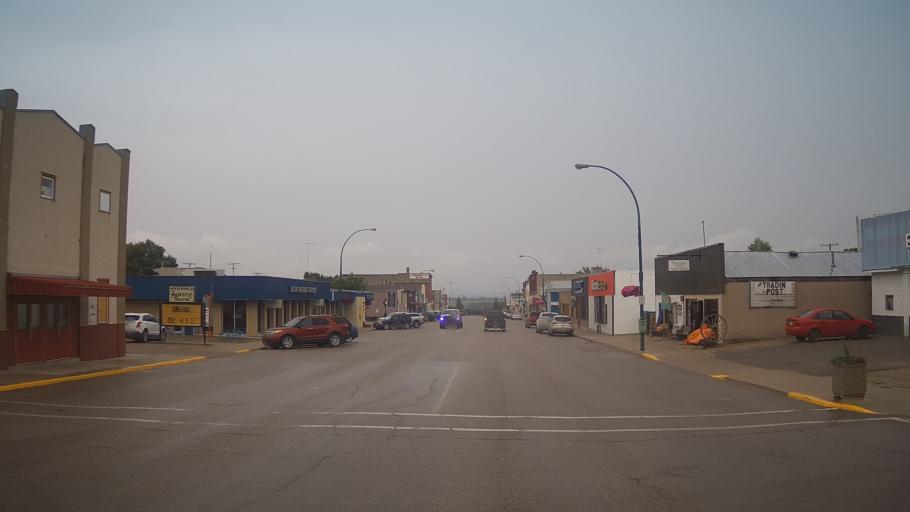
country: CA
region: Saskatchewan
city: Biggar
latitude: 52.0568
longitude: -107.9846
